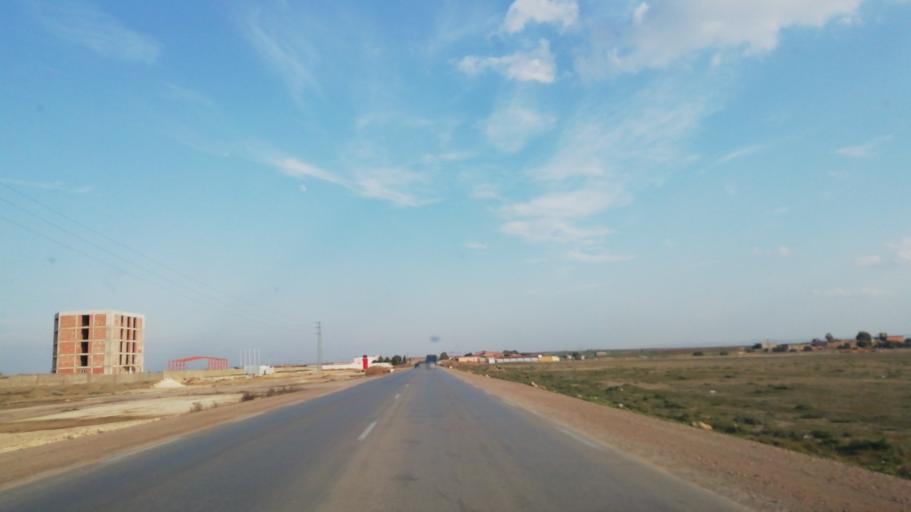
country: DZ
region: Relizane
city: Relizane
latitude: 35.8980
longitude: 0.5816
